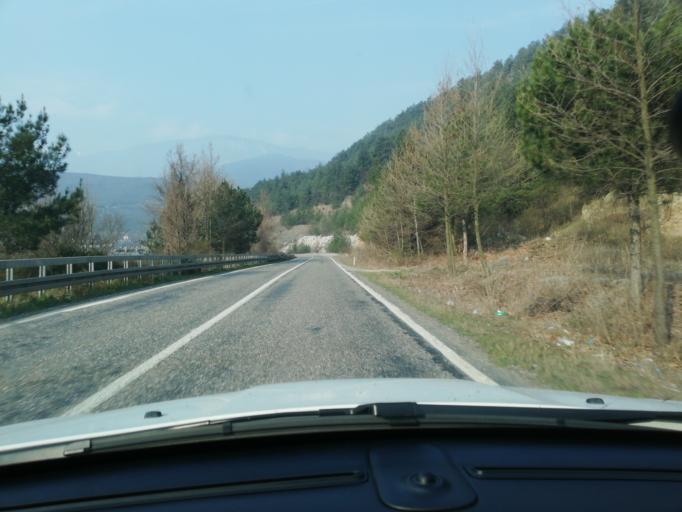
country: TR
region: Karabuk
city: Karabuk
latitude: 41.1585
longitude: 32.5457
